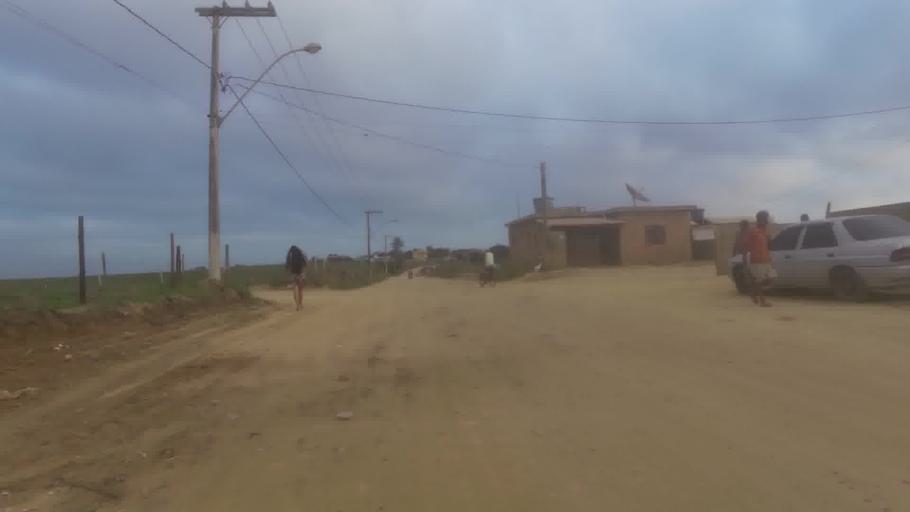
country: BR
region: Espirito Santo
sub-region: Itapemirim
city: Itapemirim
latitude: -21.0247
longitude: -40.8212
